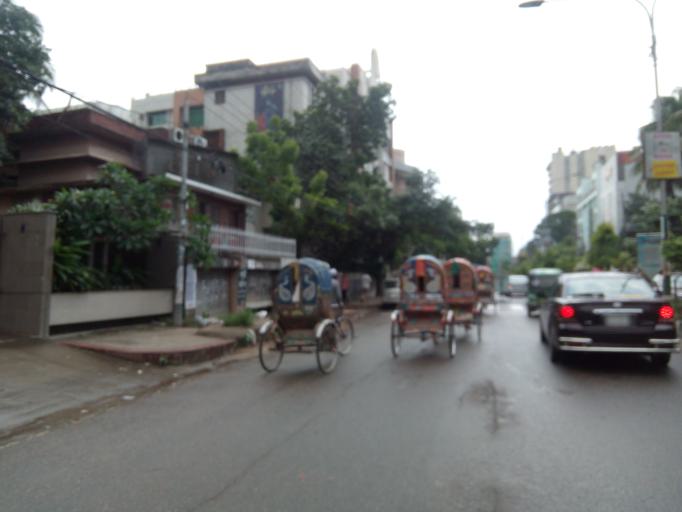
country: BD
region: Dhaka
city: Azimpur
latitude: 23.7538
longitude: 90.3712
